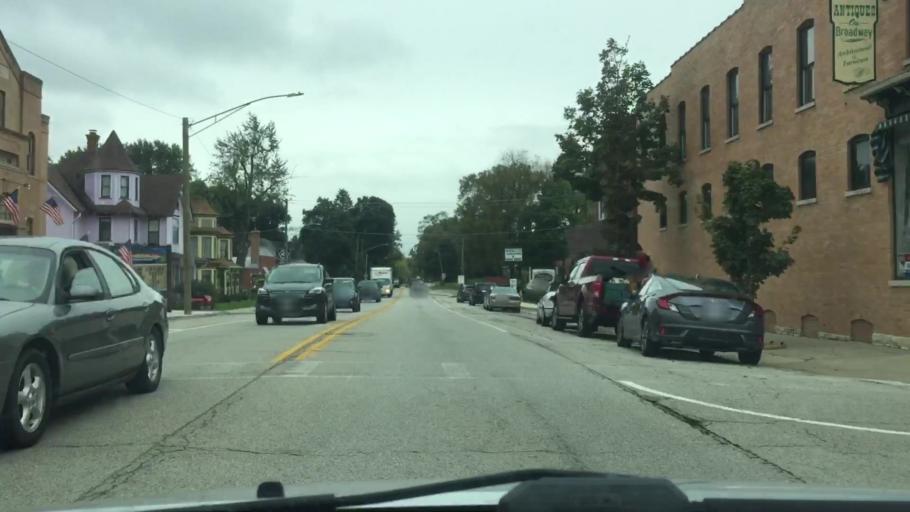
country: US
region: Illinois
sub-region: McHenry County
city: Richmond
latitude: 42.4759
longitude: -88.3061
